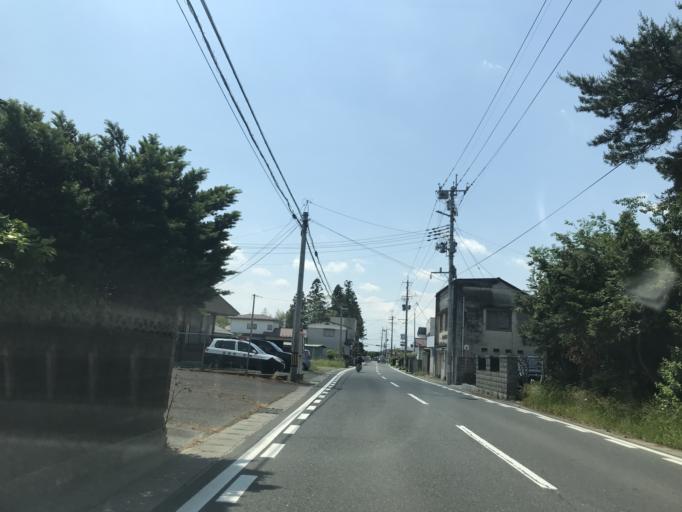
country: JP
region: Miyagi
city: Kogota
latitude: 38.5786
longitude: 141.0329
